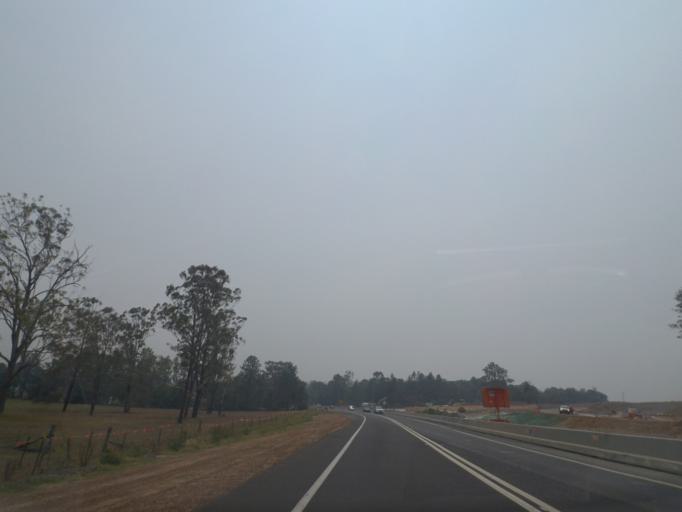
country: AU
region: New South Wales
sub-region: Clarence Valley
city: Maclean
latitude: -29.5504
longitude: 153.1553
